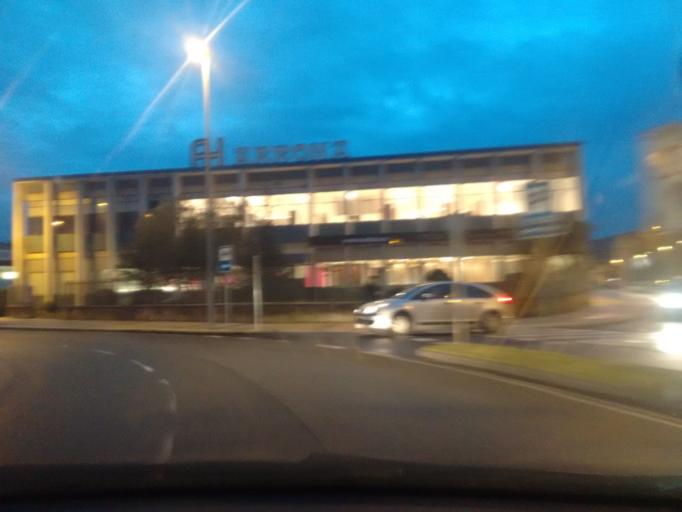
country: ES
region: Basque Country
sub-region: Provincia de Guipuzcoa
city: Zarautz
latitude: 43.2829
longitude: -2.1610
